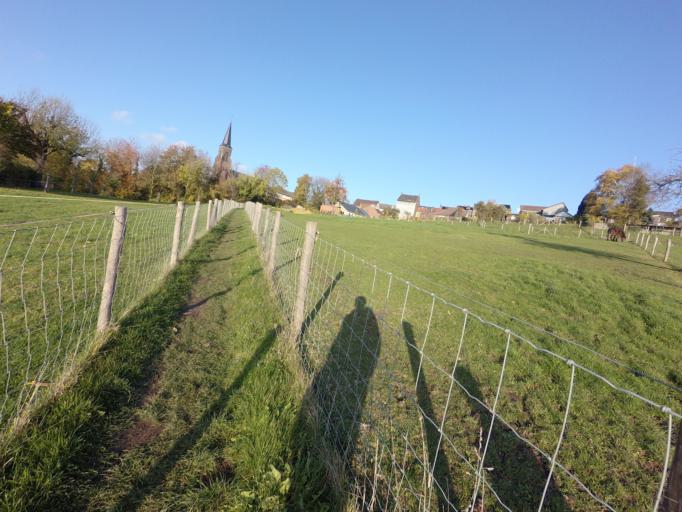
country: BE
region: Wallonia
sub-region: Province de Liege
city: Plombieres
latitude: 50.7857
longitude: 5.9623
